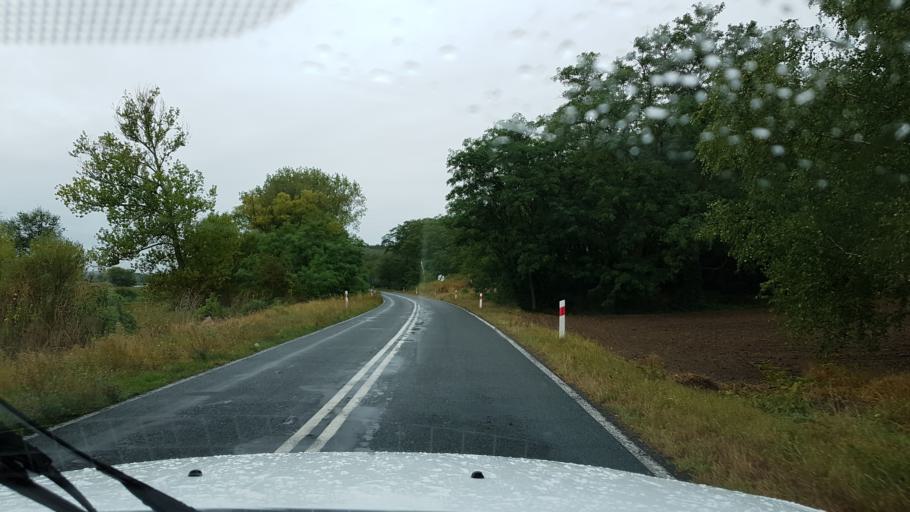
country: PL
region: West Pomeranian Voivodeship
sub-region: Powiat gryfinski
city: Cedynia
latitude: 52.8320
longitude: 14.1707
